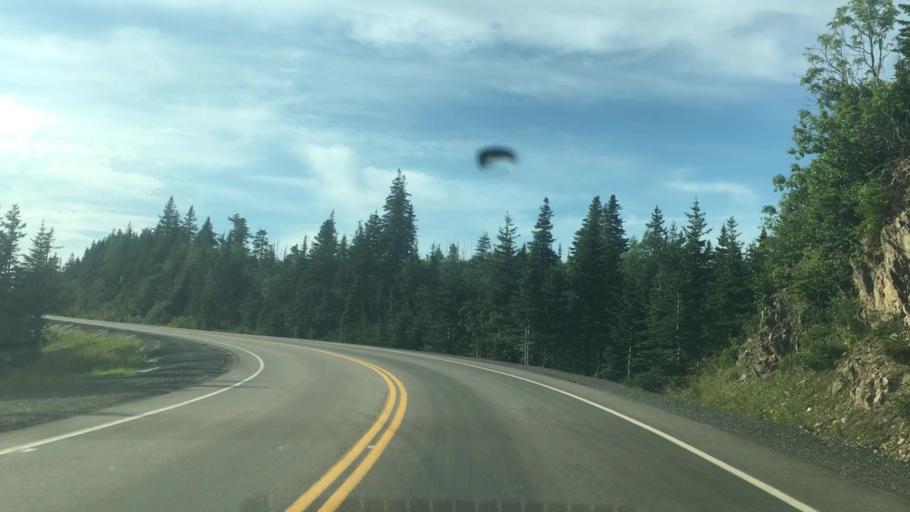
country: CA
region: Nova Scotia
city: Sydney Mines
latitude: 46.8235
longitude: -60.6556
